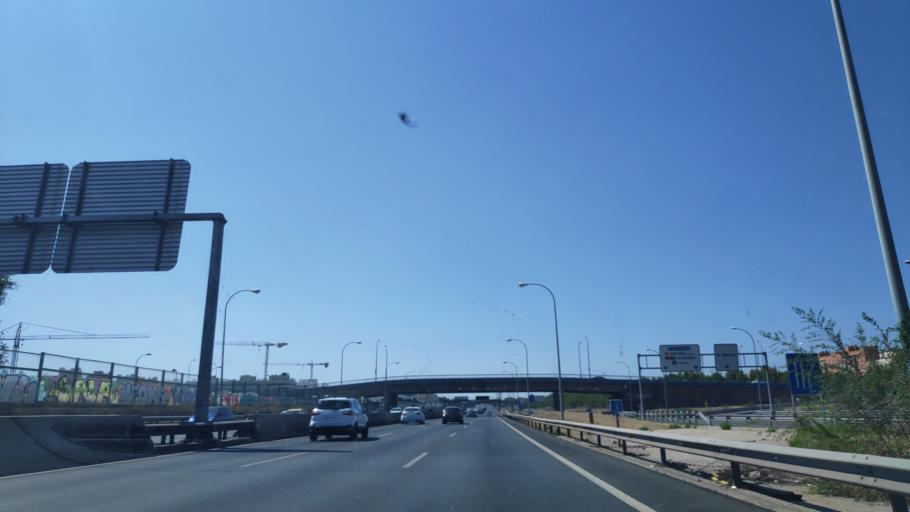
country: ES
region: Madrid
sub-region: Provincia de Madrid
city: Getafe
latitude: 40.3211
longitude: -3.7320
